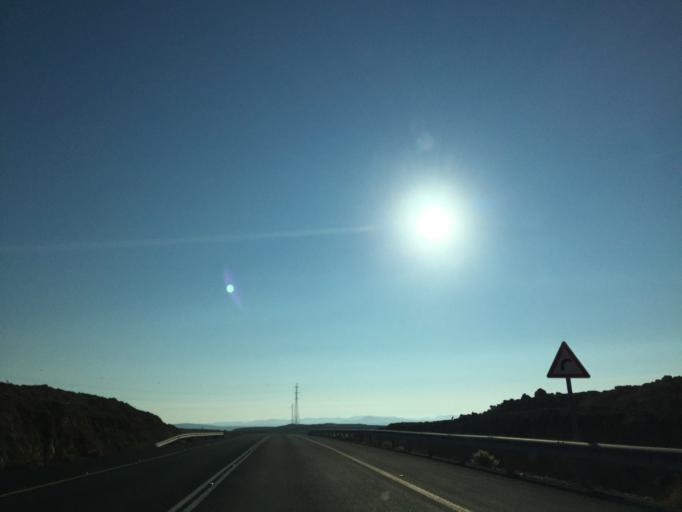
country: IL
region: Southern District
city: Mitzpe Ramon
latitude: 30.2969
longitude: 34.9786
